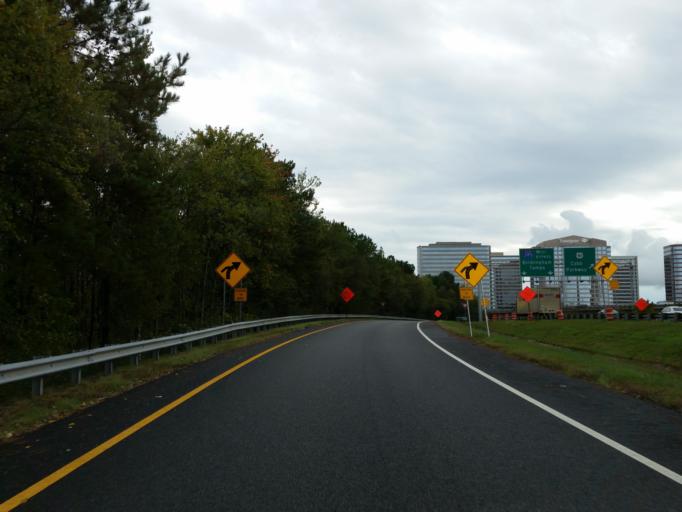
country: US
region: Georgia
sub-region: Cobb County
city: Vinings
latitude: 33.8927
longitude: -84.4632
